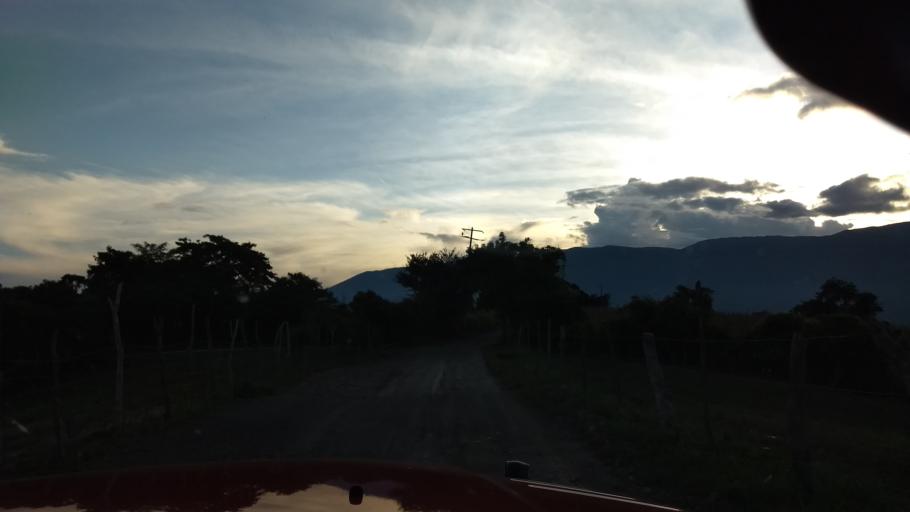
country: MX
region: Colima
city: Suchitlan
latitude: 19.4879
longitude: -103.7901
